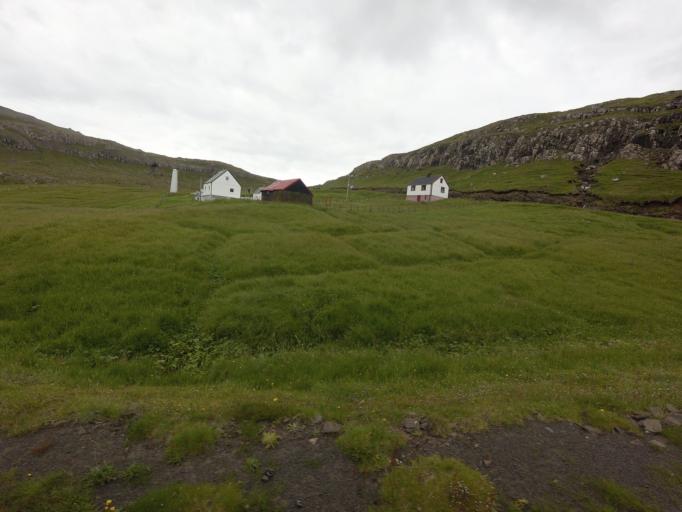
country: FO
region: Suduroy
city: Vagur
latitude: 61.4426
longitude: -6.7268
